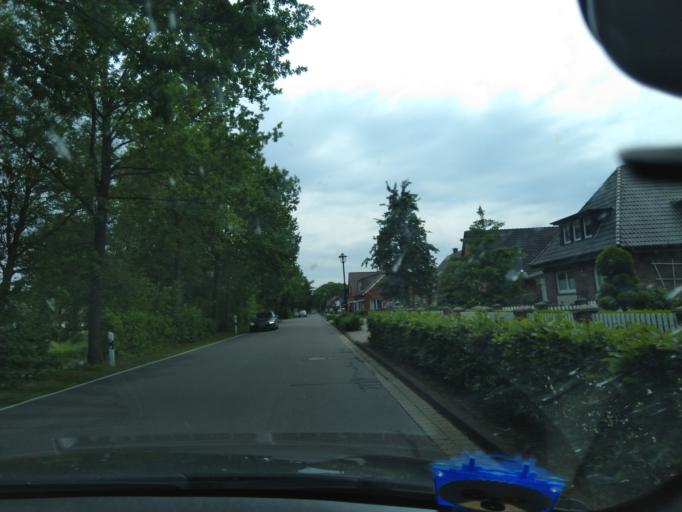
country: DE
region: Lower Saxony
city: Twist
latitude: 52.7142
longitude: 7.0996
